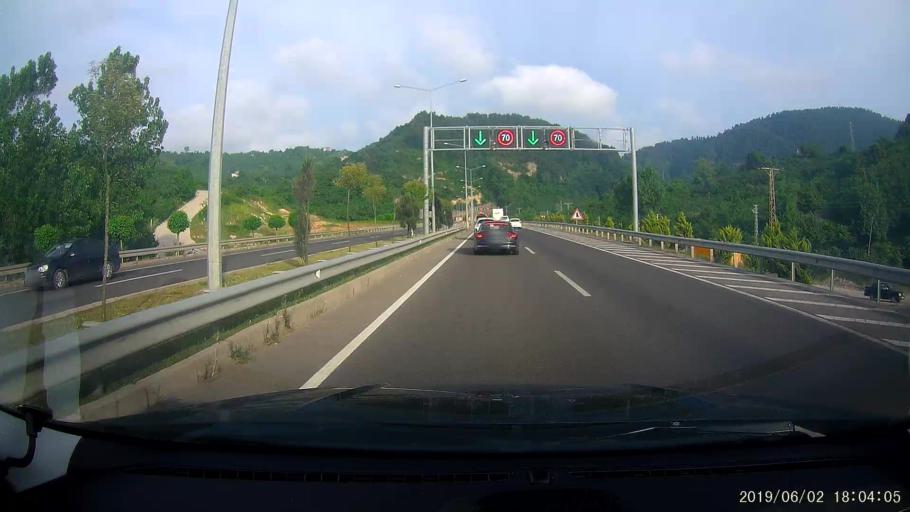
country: TR
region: Ordu
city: Unieh
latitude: 41.1229
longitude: 37.2266
